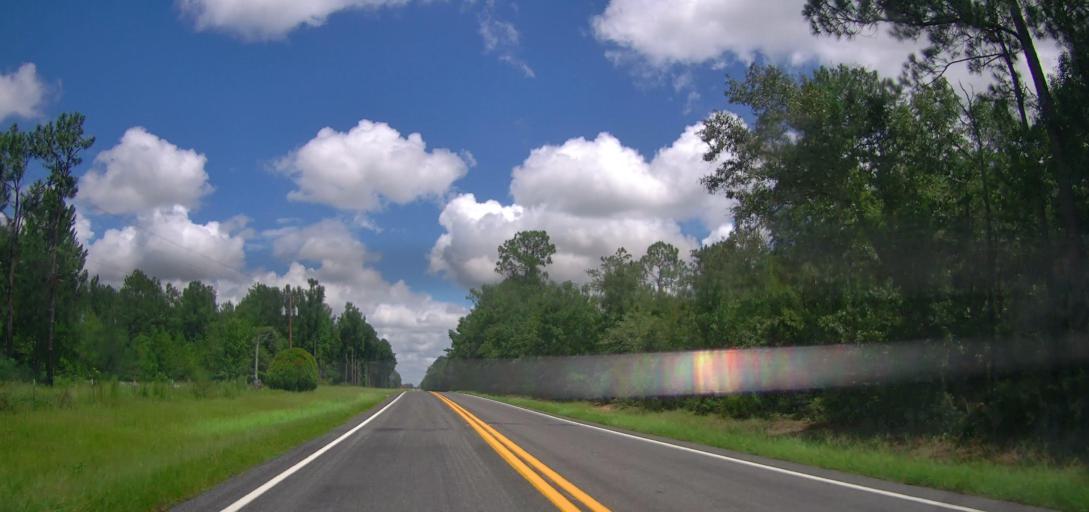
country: US
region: Georgia
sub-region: Turner County
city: Ashburn
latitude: 31.7863
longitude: -83.5984
